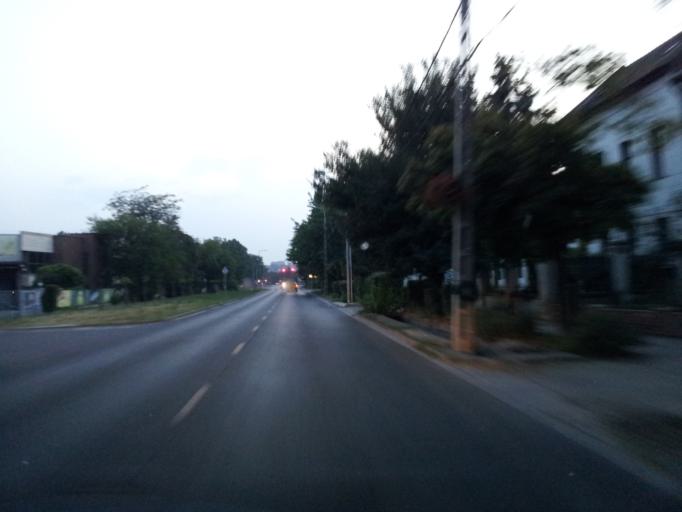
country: HU
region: Budapest
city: Budapest XXII. keruelet
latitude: 47.4118
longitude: 19.0292
